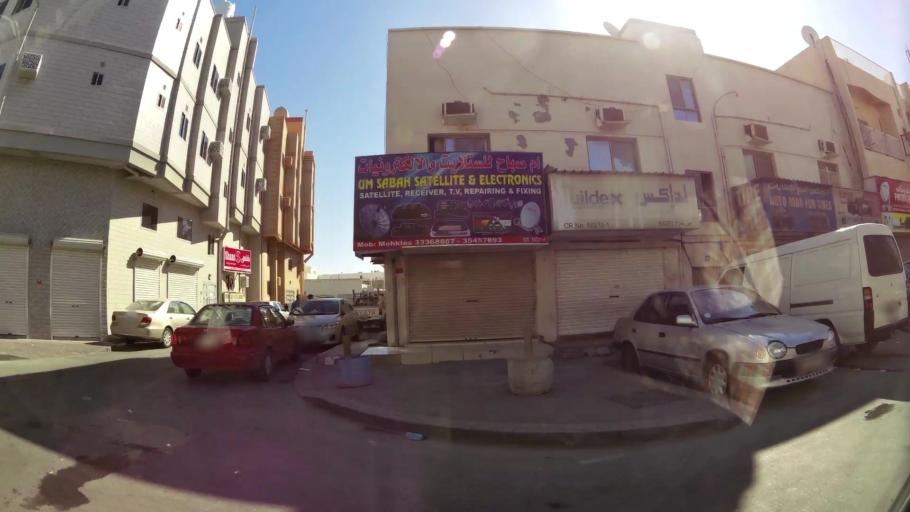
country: BH
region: Muharraq
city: Al Muharraq
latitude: 26.2542
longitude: 50.6186
